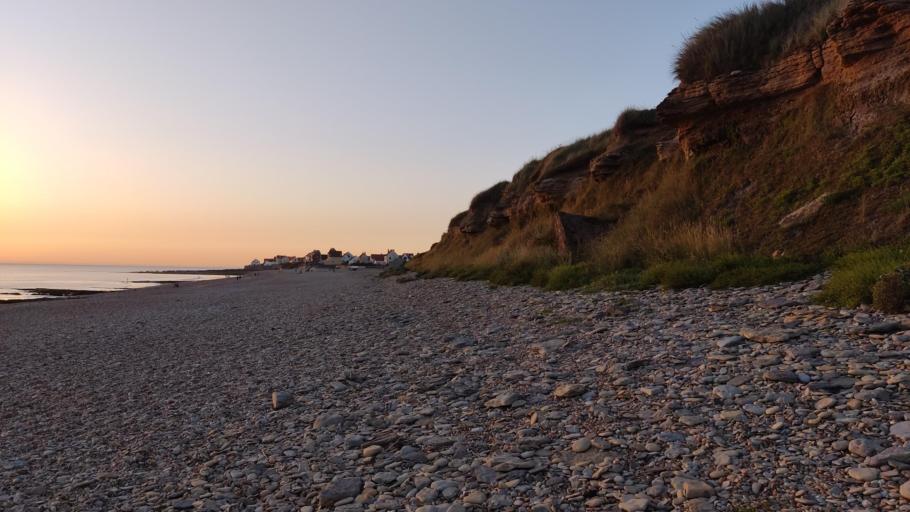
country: FR
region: Nord-Pas-de-Calais
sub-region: Departement du Pas-de-Calais
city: Ambleteuse
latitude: 50.8171
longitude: 1.5952
